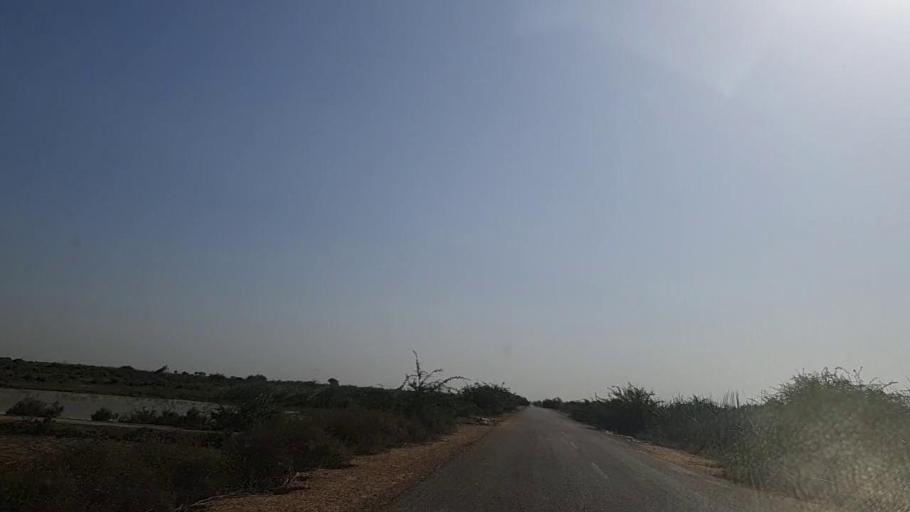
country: PK
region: Sindh
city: Jati
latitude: 24.4459
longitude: 68.2624
